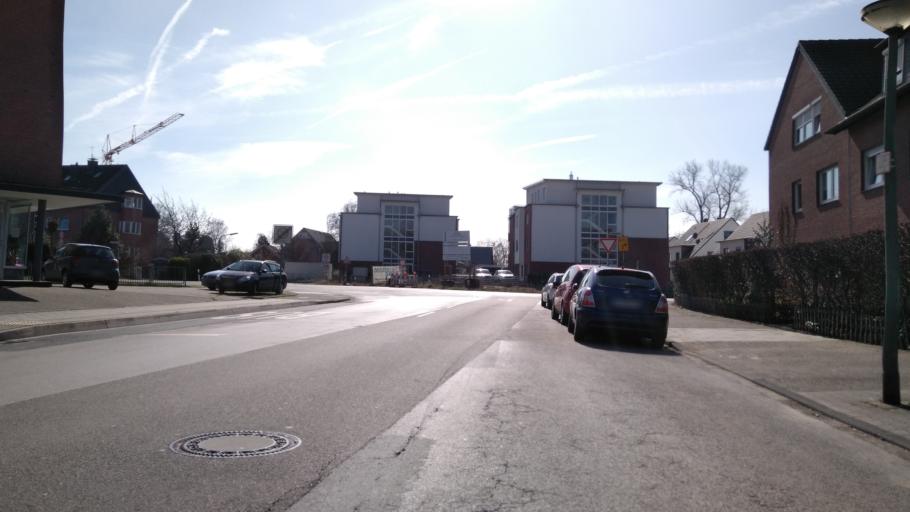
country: DE
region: North Rhine-Westphalia
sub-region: Regierungsbezirk Munster
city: Gladbeck
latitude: 51.6013
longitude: 6.9302
